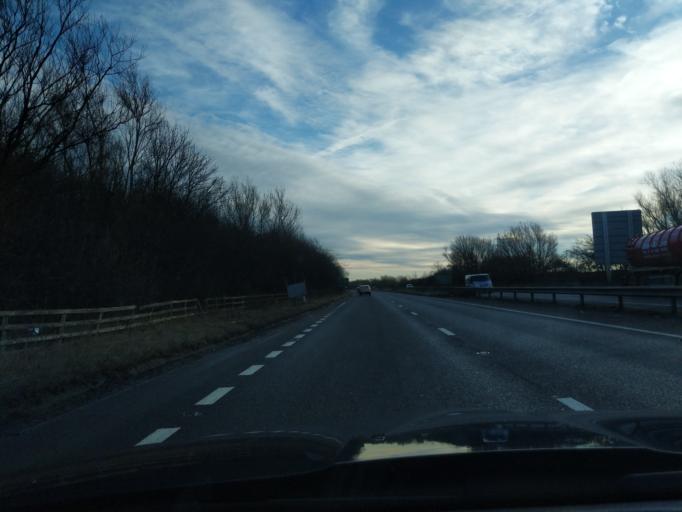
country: GB
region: England
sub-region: Borough of North Tyneside
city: Shiremoor
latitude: 55.0250
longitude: -1.5194
